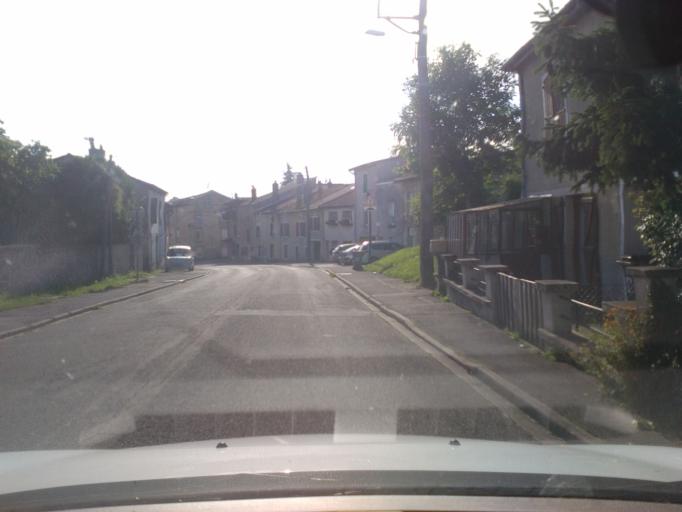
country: FR
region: Lorraine
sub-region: Departement des Vosges
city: Mirecourt
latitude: 48.3007
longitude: 6.1412
